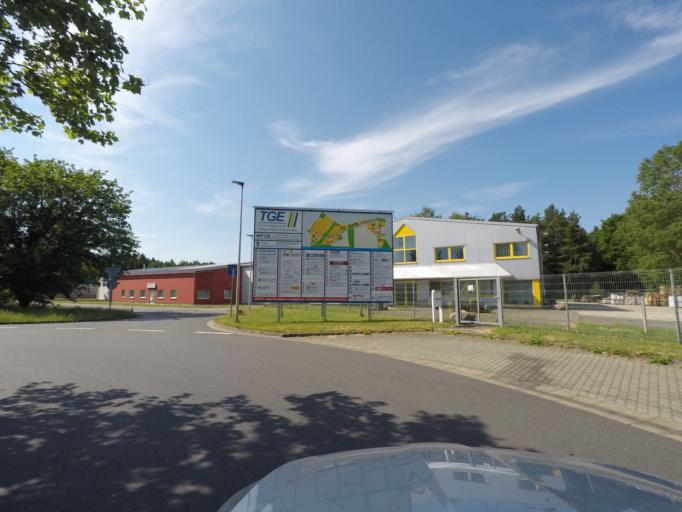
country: DE
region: Brandenburg
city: Britz
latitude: 52.8593
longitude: 13.7882
